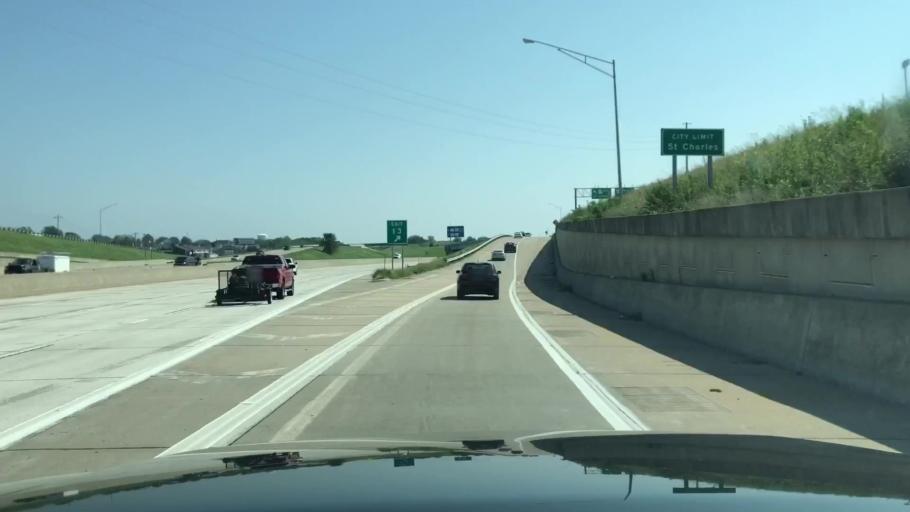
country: US
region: Missouri
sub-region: Saint Charles County
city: Saint Charles
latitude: 38.7531
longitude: -90.5527
